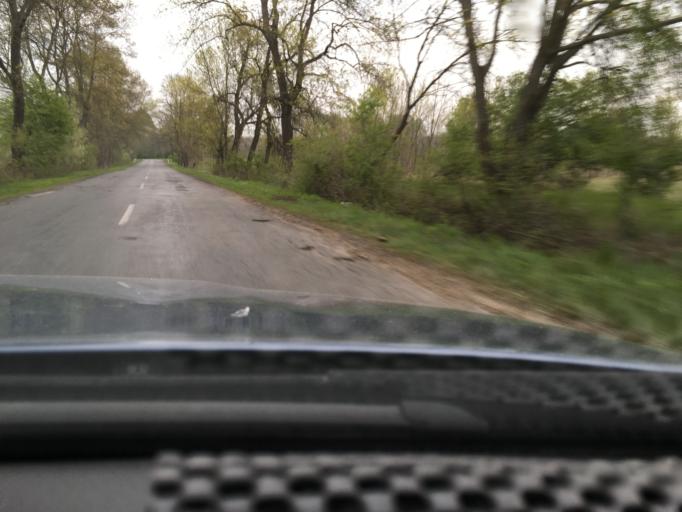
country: HU
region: Szabolcs-Szatmar-Bereg
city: Nyirbeltek
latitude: 47.6900
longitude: 22.0994
